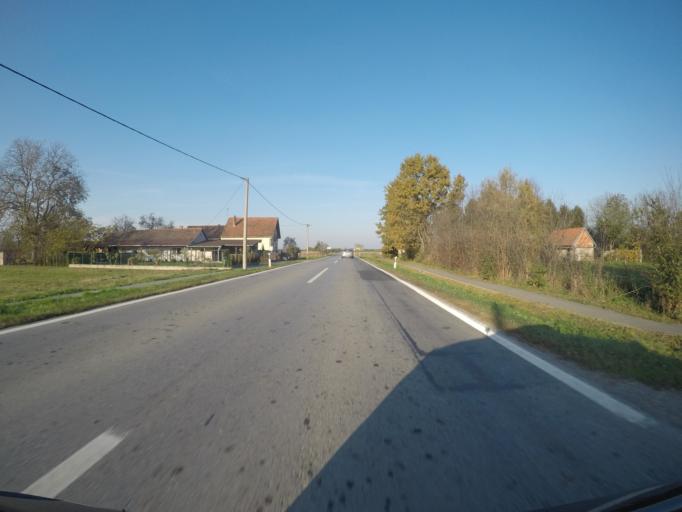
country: HU
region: Somogy
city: Barcs
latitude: 45.9148
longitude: 17.4472
